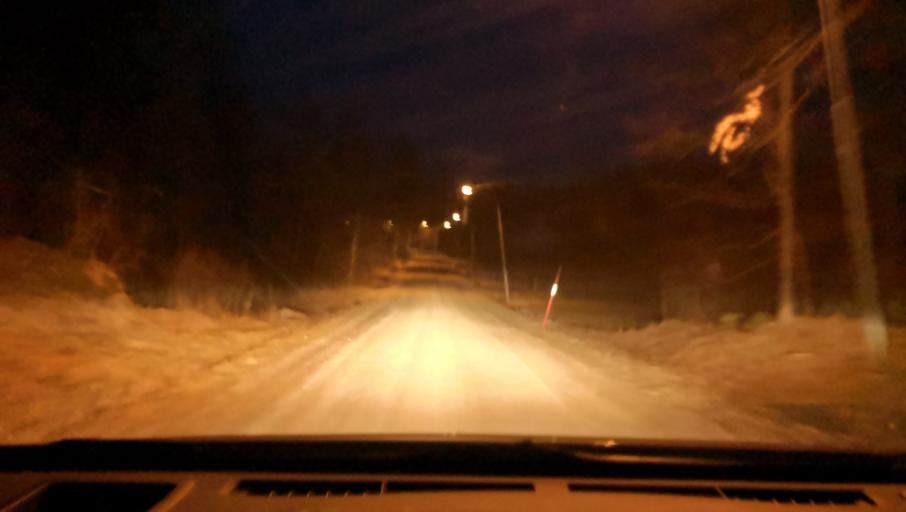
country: SE
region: Vaestmanland
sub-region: Skinnskattebergs Kommun
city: Skinnskatteberg
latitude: 59.6636
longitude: 15.5295
